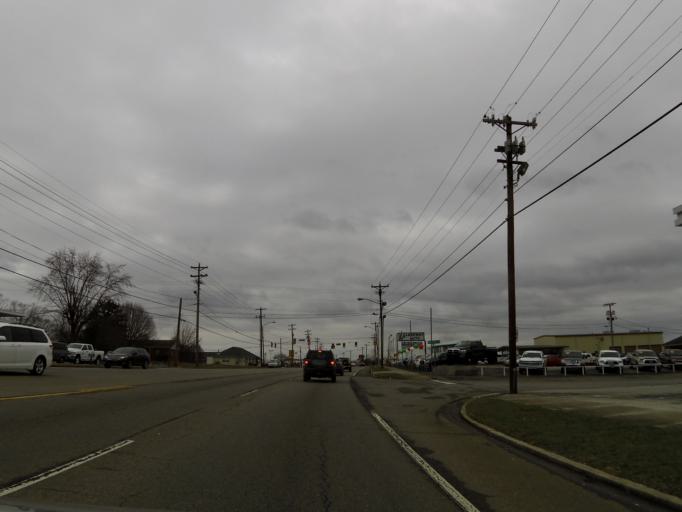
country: US
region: Tennessee
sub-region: Hamblen County
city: Morristown
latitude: 36.2002
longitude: -83.3391
